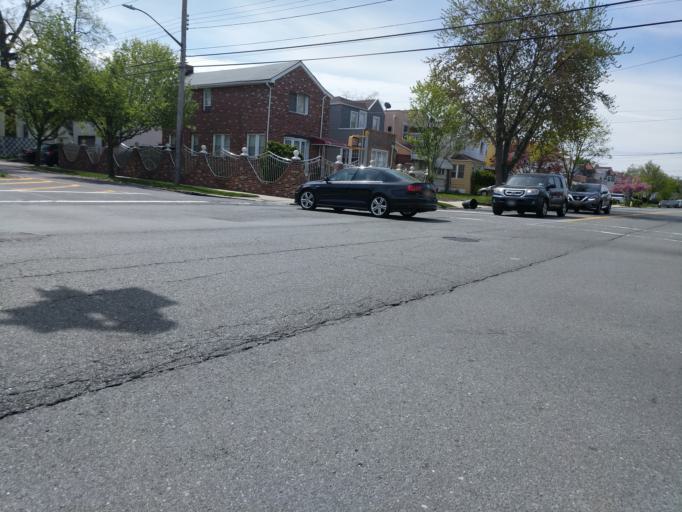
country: US
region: New York
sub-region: Nassau County
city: South Valley Stream
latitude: 40.6743
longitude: -73.7405
